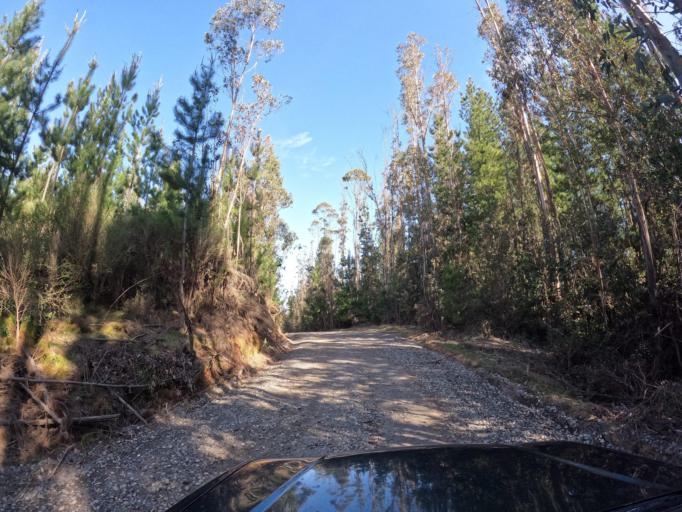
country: CL
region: Biobio
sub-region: Provincia de Biobio
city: La Laja
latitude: -37.0856
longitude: -72.7776
